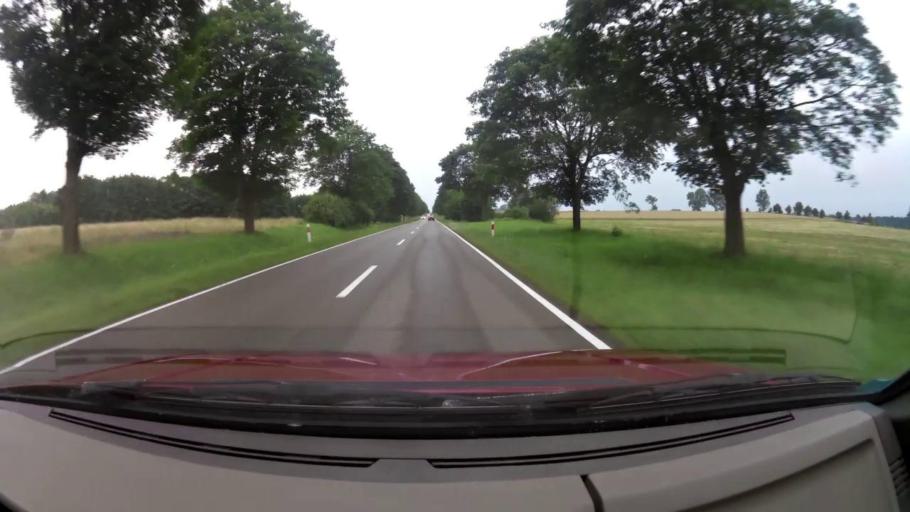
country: PL
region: West Pomeranian Voivodeship
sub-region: Powiat stargardzki
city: Stara Dabrowa
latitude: 53.3934
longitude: 15.1969
